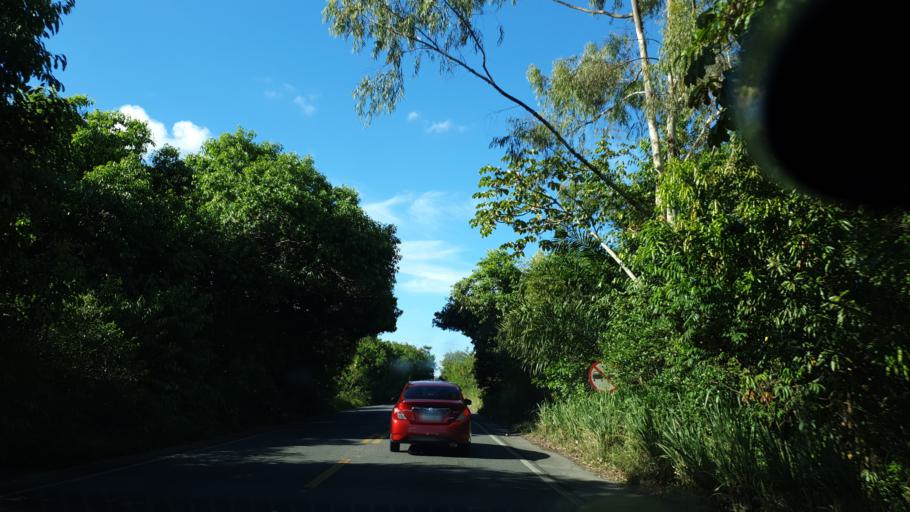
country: BR
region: Bahia
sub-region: Camacari
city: Camacari
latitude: -12.6471
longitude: -38.3041
